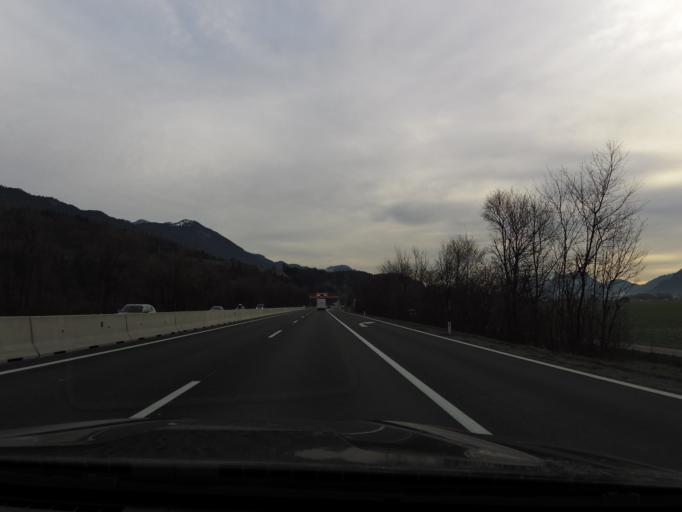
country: AT
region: Tyrol
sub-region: Politischer Bezirk Kufstein
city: Radfeld
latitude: 47.4538
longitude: 11.9134
